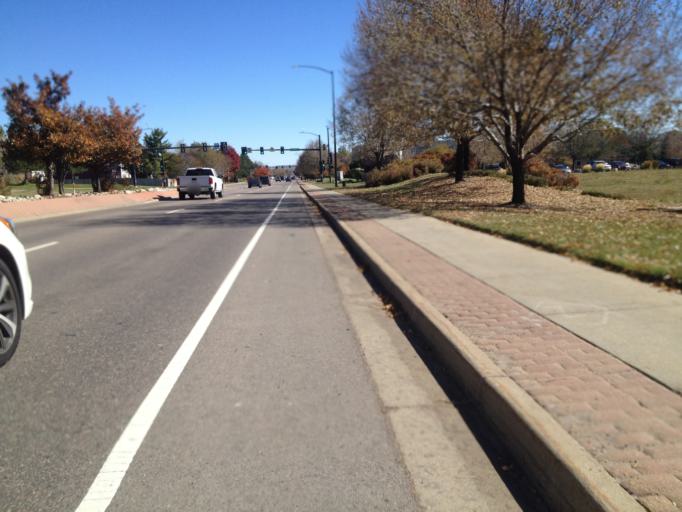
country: US
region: Colorado
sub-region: Boulder County
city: Lafayette
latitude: 39.9868
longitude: -105.1048
